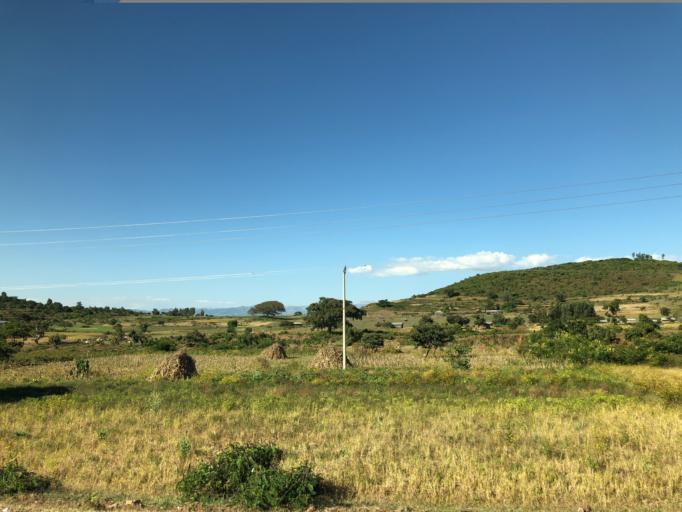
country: ET
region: Amhara
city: Werota
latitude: 11.9368
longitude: 37.7837
